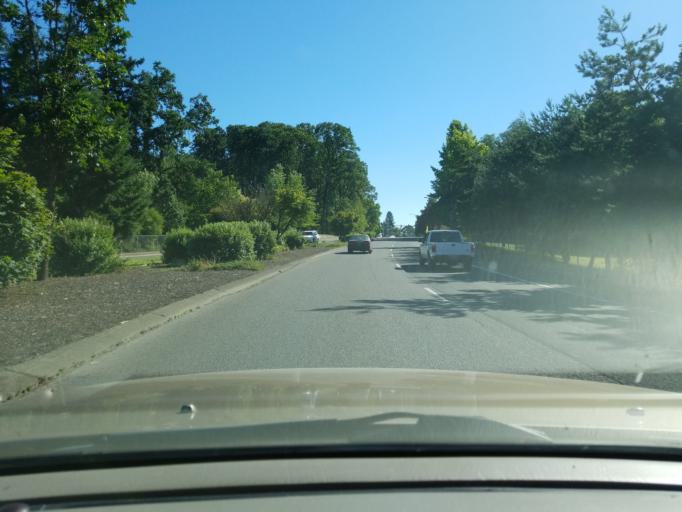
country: US
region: Oregon
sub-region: Yamhill County
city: McMinnville
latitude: 45.2039
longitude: -123.2000
